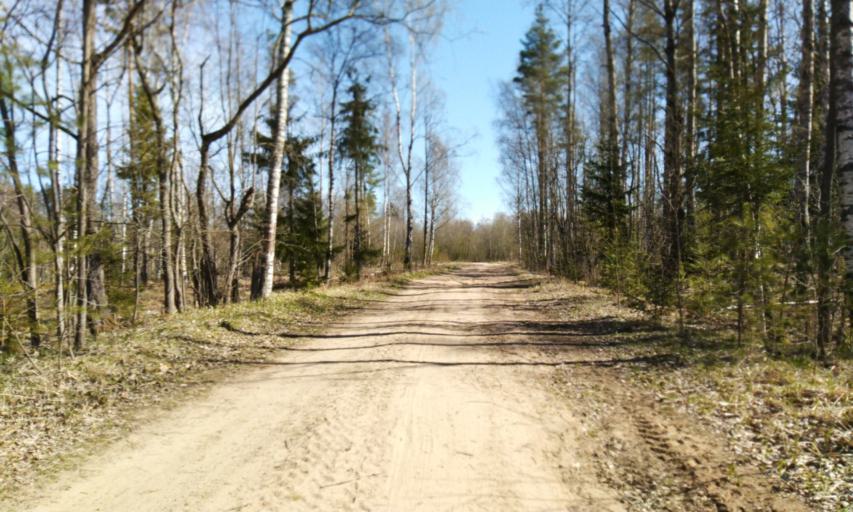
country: RU
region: Leningrad
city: Garbolovo
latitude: 60.4212
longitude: 30.4677
